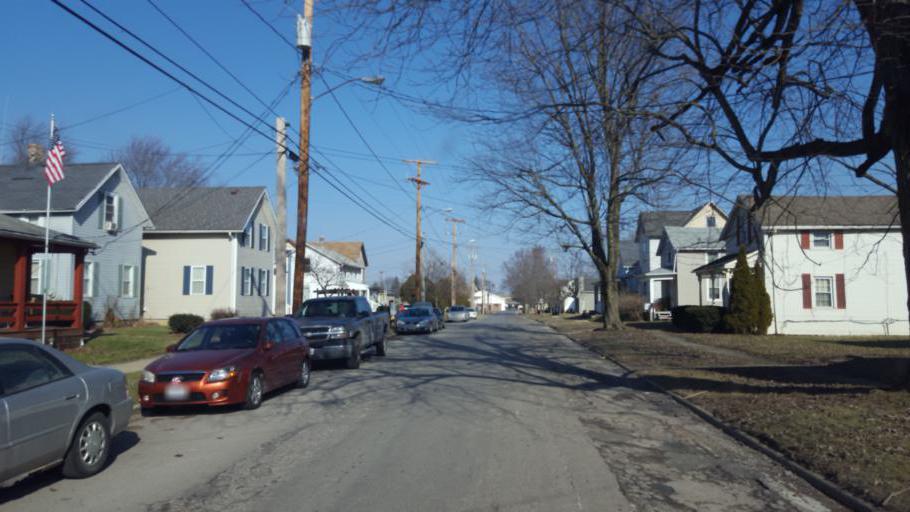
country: US
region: Ohio
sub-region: Crawford County
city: Galion
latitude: 40.7313
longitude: -82.7835
